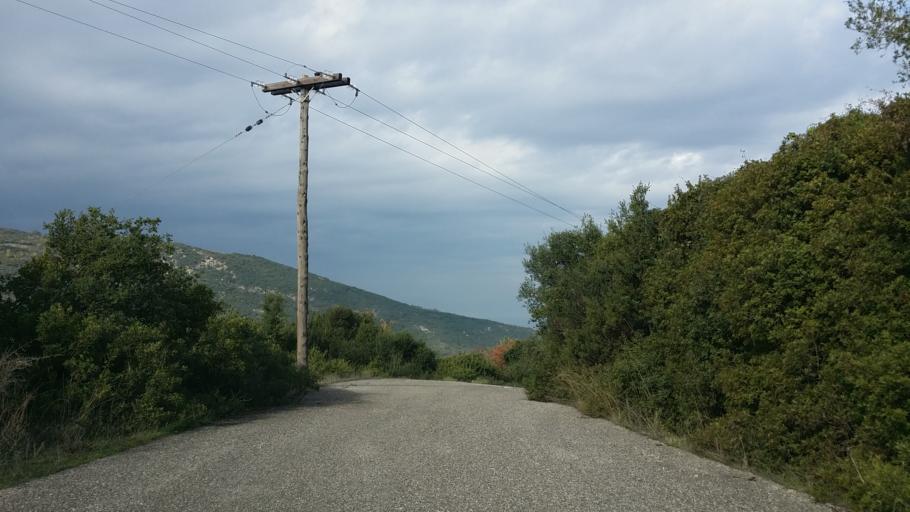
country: GR
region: West Greece
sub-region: Nomos Aitolias kai Akarnanias
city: Katouna
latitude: 38.8523
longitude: 21.0557
